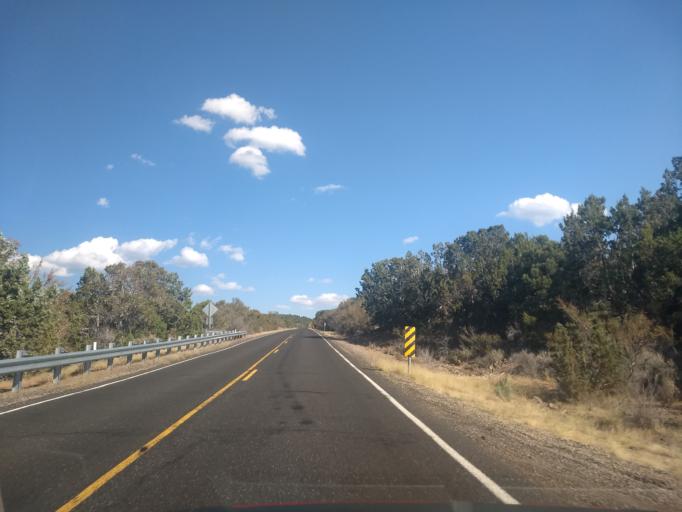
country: US
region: Utah
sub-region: Washington County
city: Enterprise
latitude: 37.4235
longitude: -113.5814
